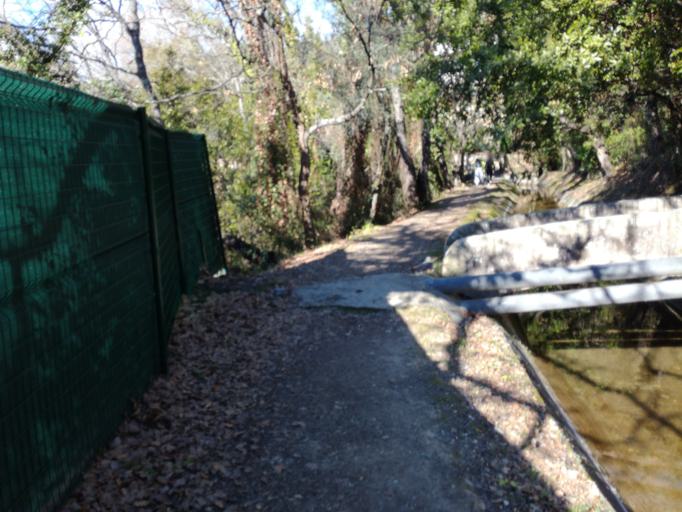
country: FR
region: Provence-Alpes-Cote d'Azur
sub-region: Departement des Alpes-Maritimes
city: Mouans-Sartoux
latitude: 43.6278
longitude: 6.9797
